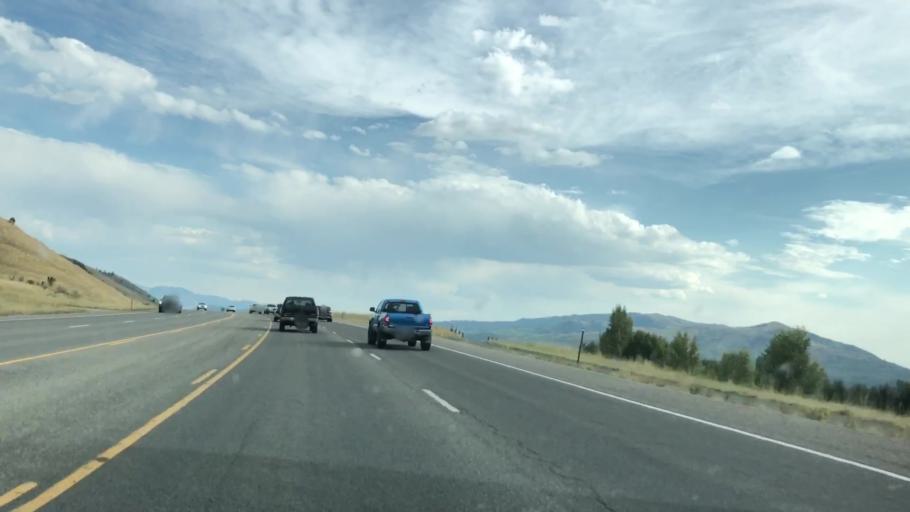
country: US
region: Wyoming
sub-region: Teton County
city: South Park
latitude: 43.4358
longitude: -110.7860
